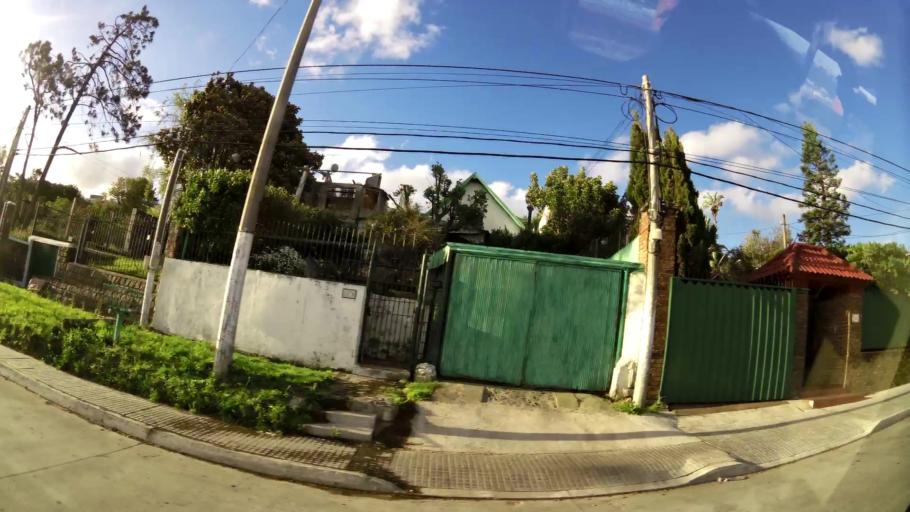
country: UY
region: Montevideo
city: Montevideo
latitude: -34.8954
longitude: -56.2532
